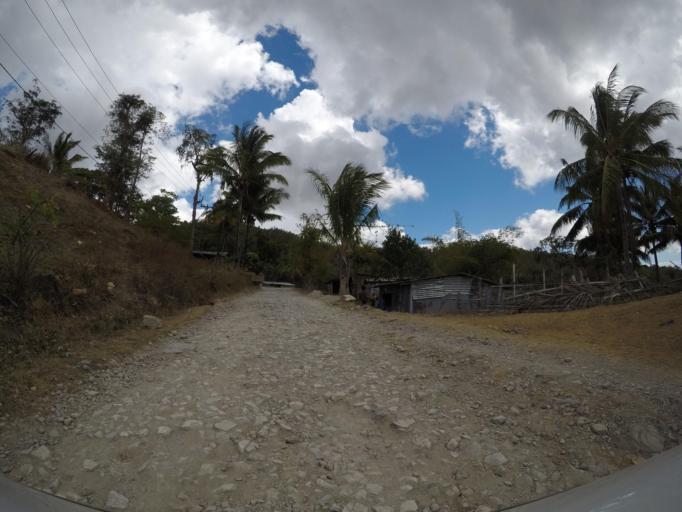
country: TL
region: Baucau
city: Baucau
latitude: -8.5072
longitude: 126.6789
